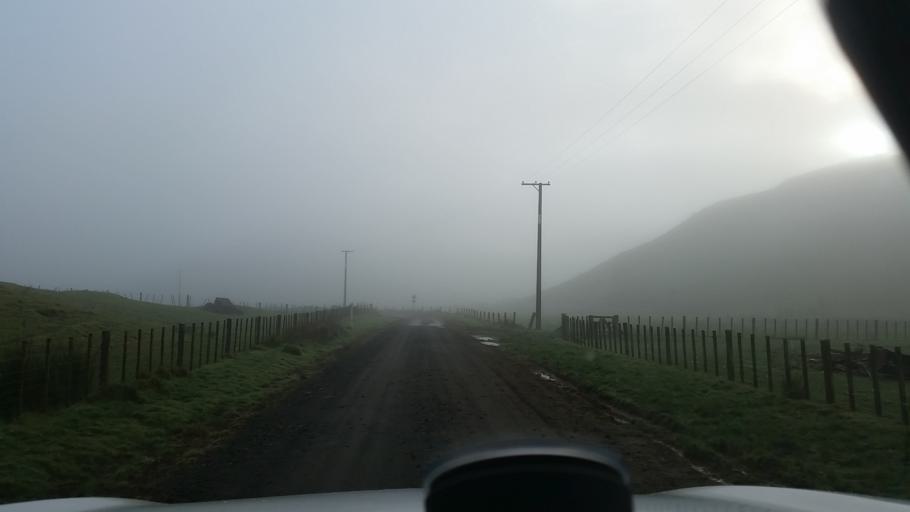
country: NZ
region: Taranaki
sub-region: South Taranaki District
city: Eltham
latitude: -39.4050
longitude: 174.4310
